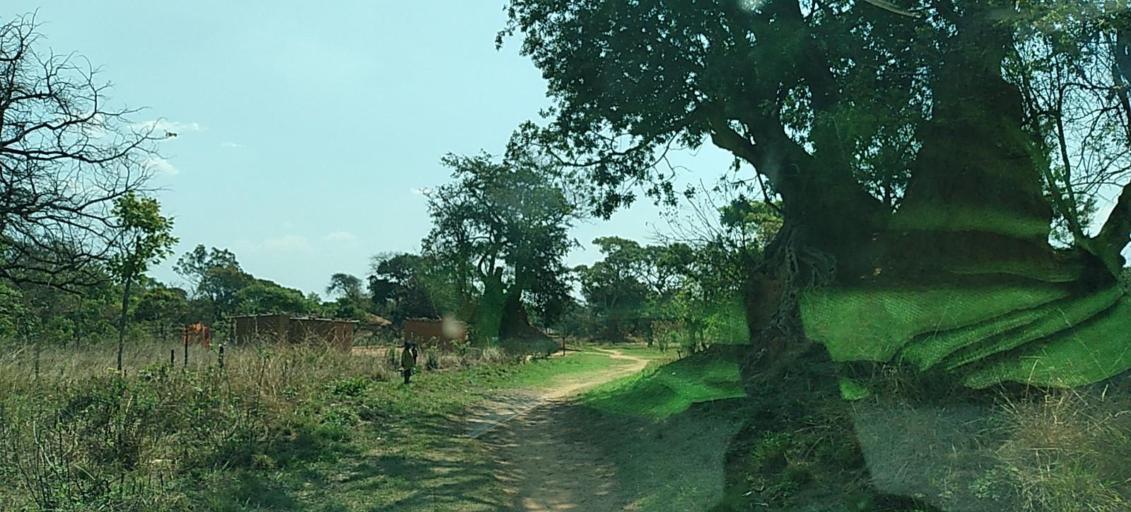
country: CD
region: Katanga
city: Kolwezi
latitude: -11.2786
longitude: 25.1244
